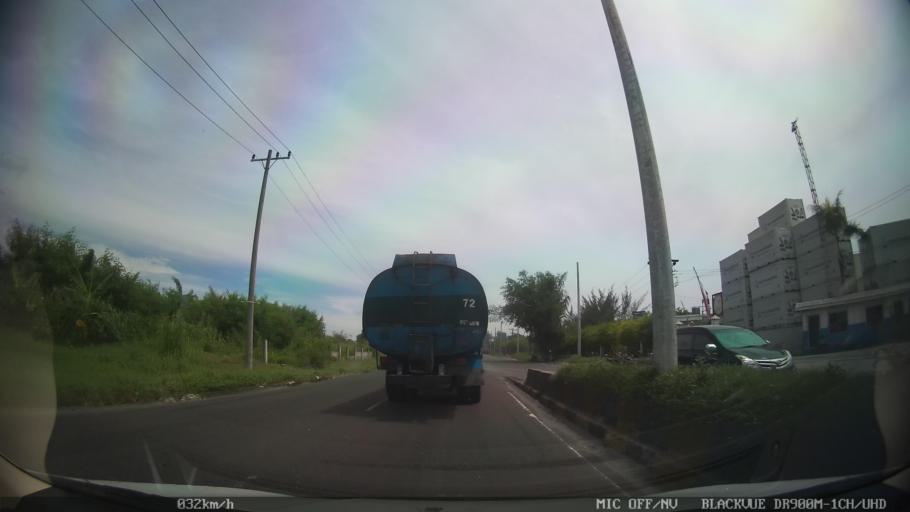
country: ID
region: North Sumatra
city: Belawan
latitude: 3.7731
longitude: 98.6857
